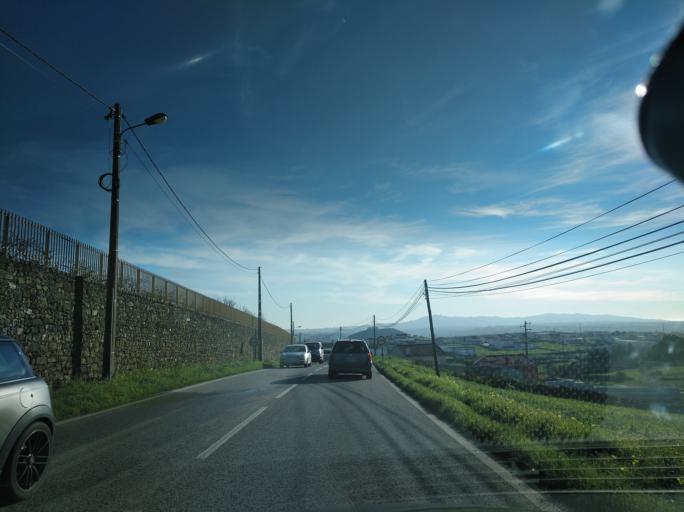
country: PT
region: Lisbon
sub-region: Mafra
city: Mafra
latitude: 38.9200
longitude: -9.3223
